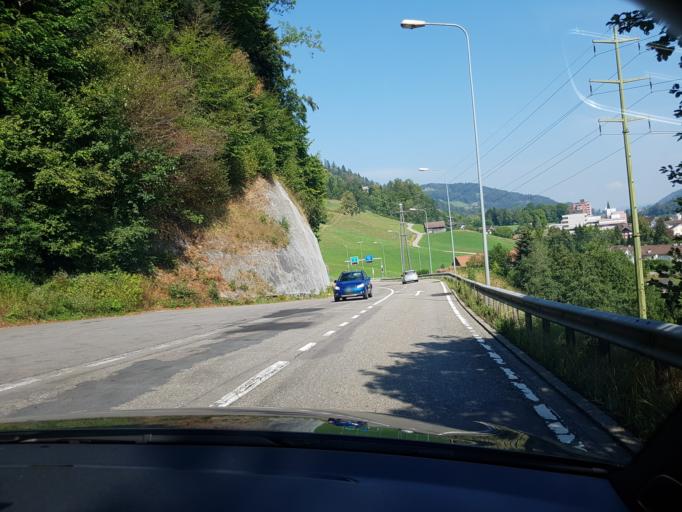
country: CH
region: Saint Gallen
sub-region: Wahlkreis Toggenburg
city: Wattwil
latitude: 47.2931
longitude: 9.0851
